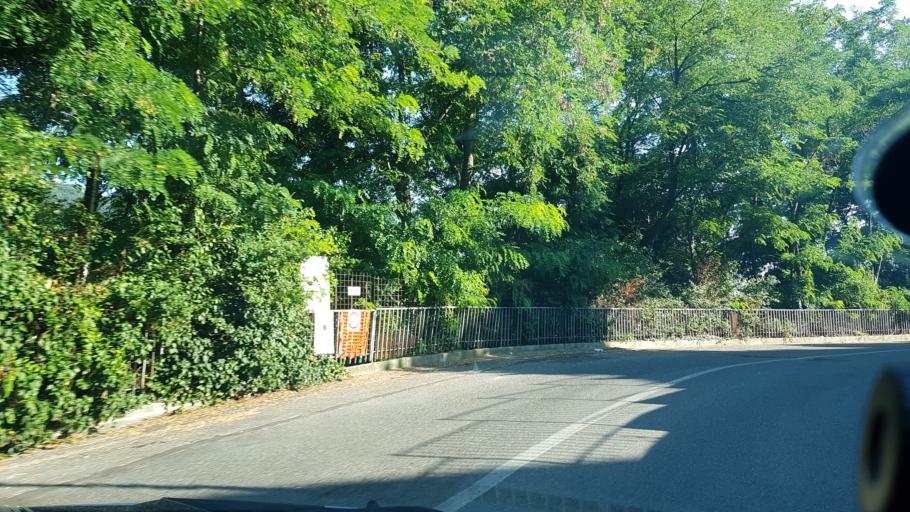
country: IT
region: Liguria
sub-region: Provincia di Genova
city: Genoa
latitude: 44.4414
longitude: 8.8987
